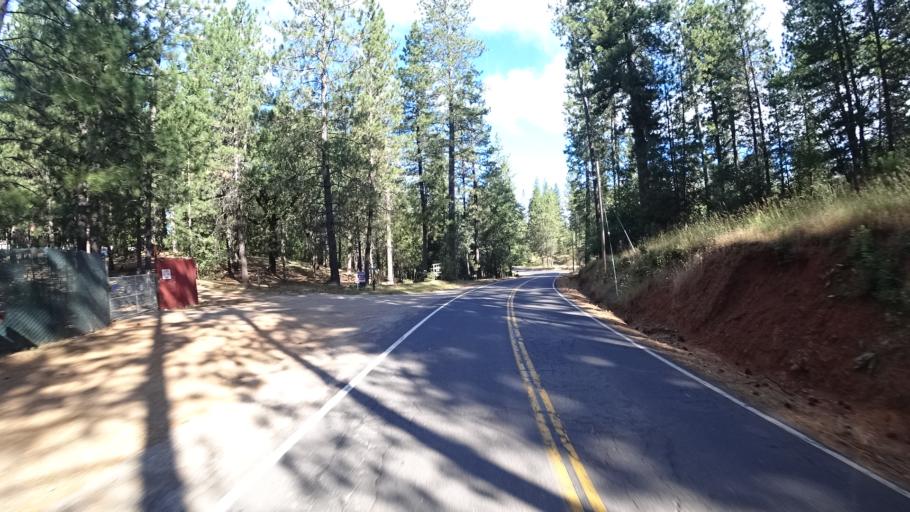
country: US
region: California
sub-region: Amador County
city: Pioneer
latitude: 38.3770
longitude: -120.4934
